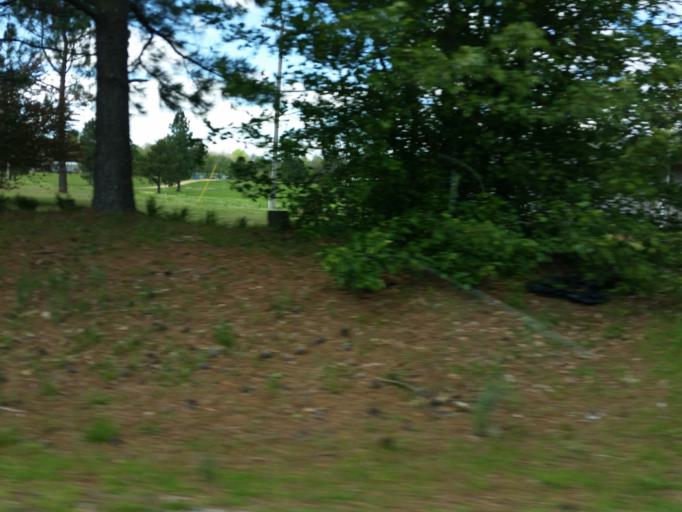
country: US
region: Arkansas
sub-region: Craighead County
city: Bono
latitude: 35.9937
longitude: -90.7092
